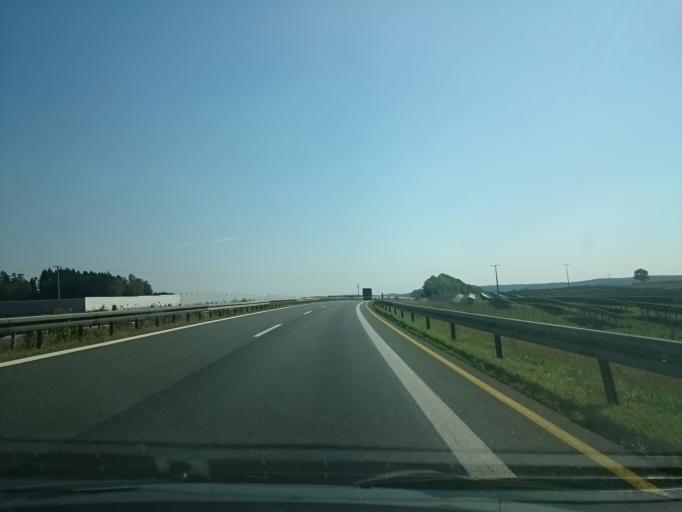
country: DE
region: Bavaria
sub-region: Upper Franconia
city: Wonsees
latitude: 50.0073
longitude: 11.2750
